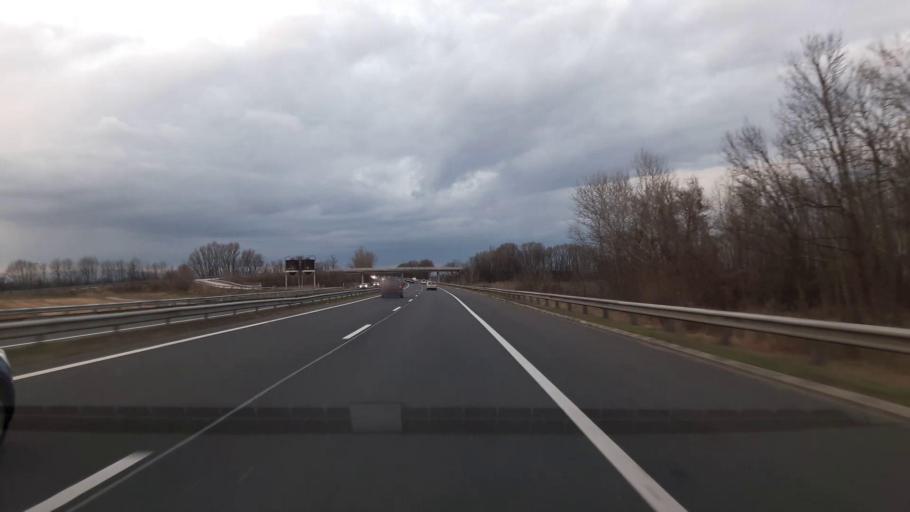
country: AT
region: Burgenland
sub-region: Eisenstadt-Umgebung
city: Wimpassing an der Leitha
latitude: 47.9042
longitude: 16.4126
